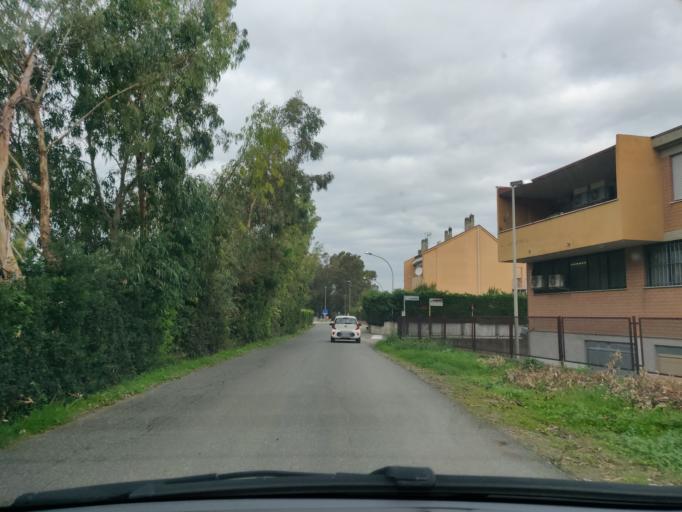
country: IT
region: Latium
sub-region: Citta metropolitana di Roma Capitale
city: Aurelia
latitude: 42.1368
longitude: 11.7824
